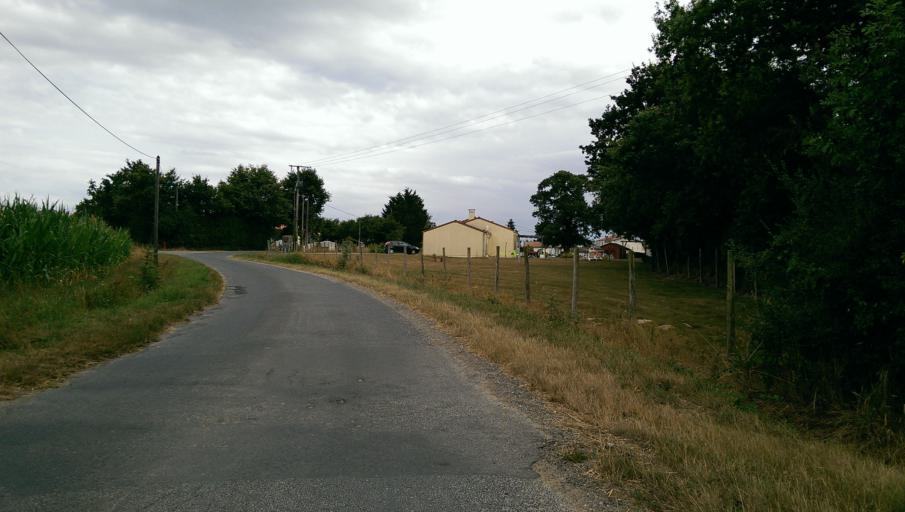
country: FR
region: Pays de la Loire
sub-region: Departement de la Loire-Atlantique
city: Vieillevigne
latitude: 46.9890
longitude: -1.4139
